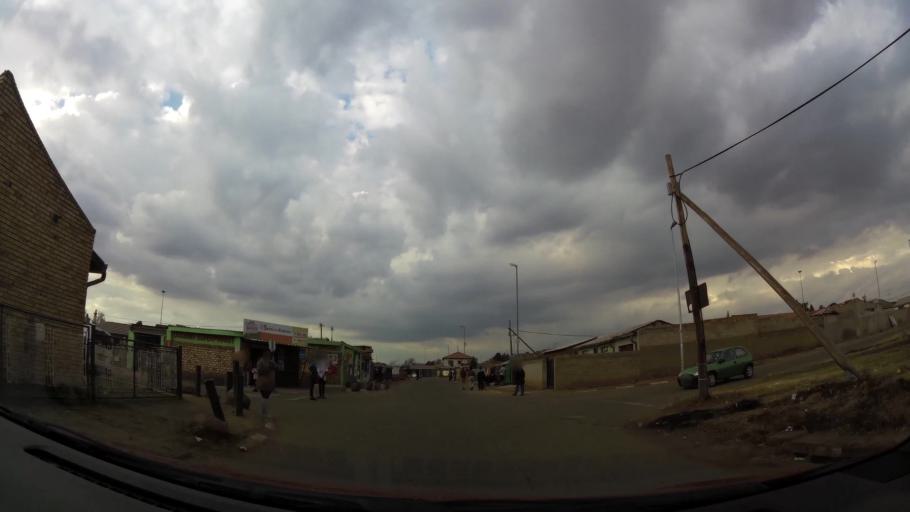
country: ZA
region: Gauteng
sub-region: City of Johannesburg Metropolitan Municipality
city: Soweto
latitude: -26.2428
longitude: 27.8191
